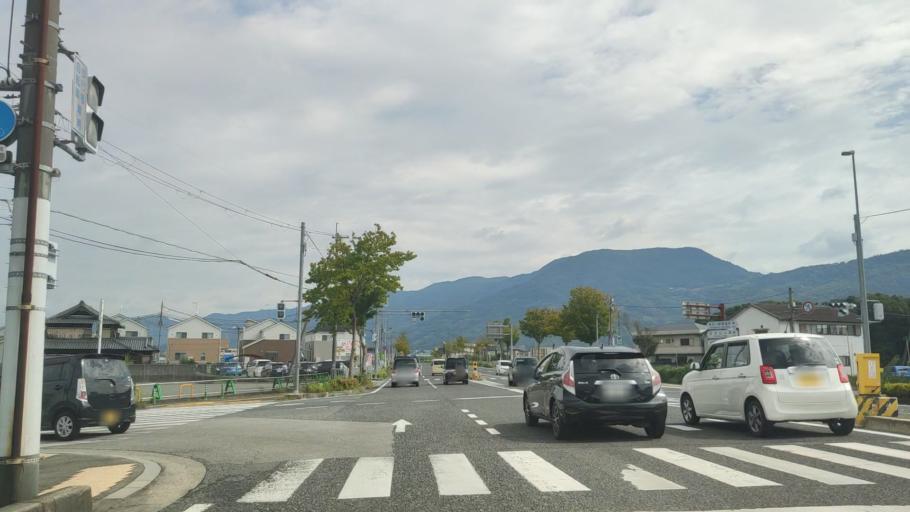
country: JP
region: Wakayama
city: Iwade
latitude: 34.2621
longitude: 135.3725
